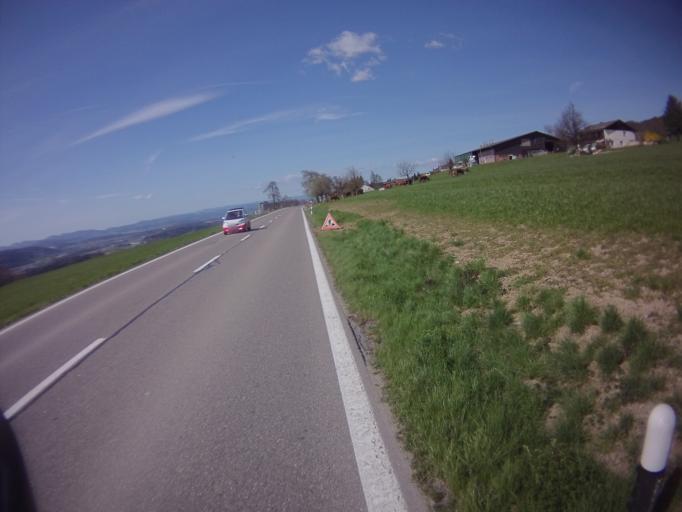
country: CH
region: Aargau
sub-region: Bezirk Baden
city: Kunten
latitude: 47.3820
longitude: 8.3493
